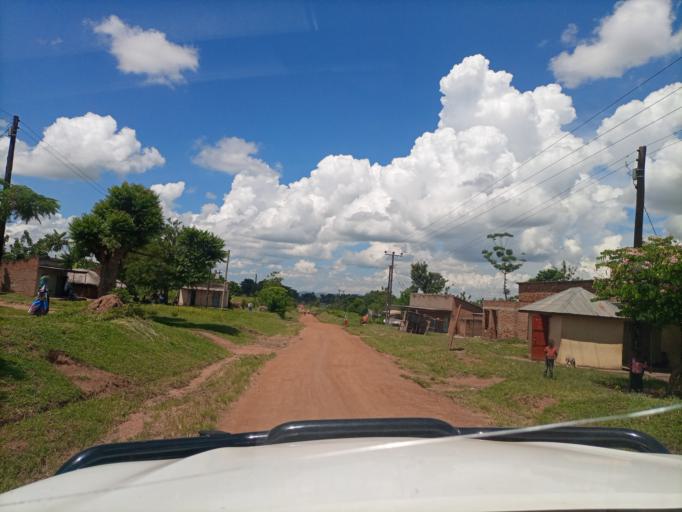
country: UG
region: Eastern Region
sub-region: Tororo District
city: Tororo
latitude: 0.6854
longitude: 34.0085
